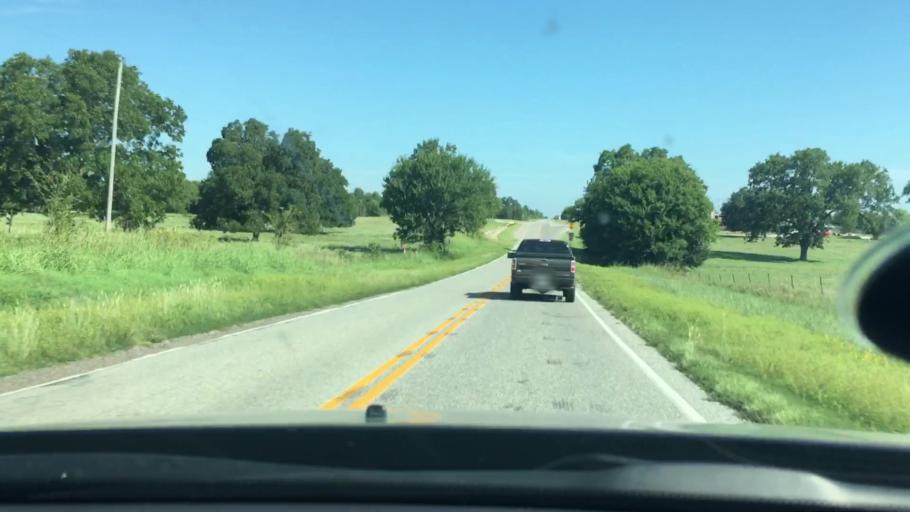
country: US
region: Oklahoma
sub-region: Johnston County
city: Tishomingo
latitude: 34.2711
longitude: -96.5487
